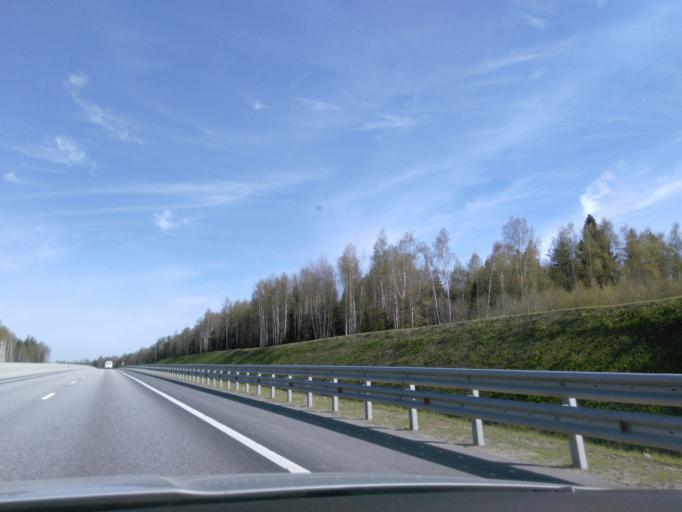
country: RU
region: Moskovskaya
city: Lozhki
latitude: 56.1265
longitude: 37.1106
